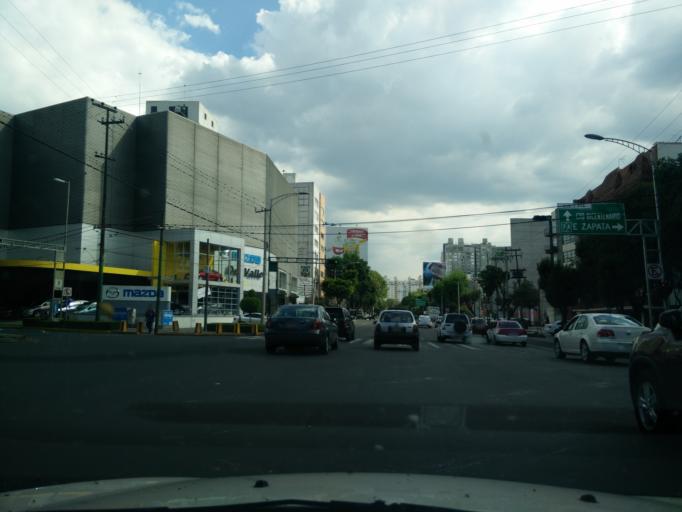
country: MX
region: Mexico City
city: Colonia del Valle
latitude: 19.3693
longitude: -99.1616
